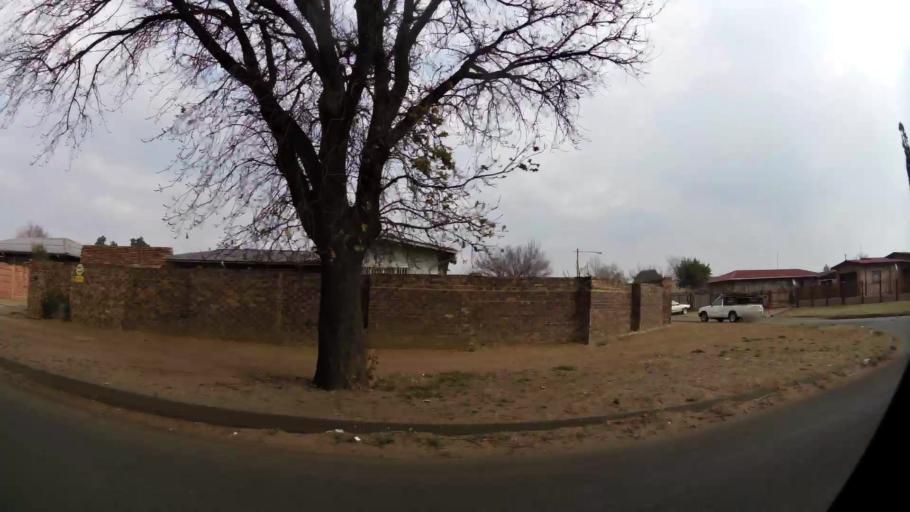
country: ZA
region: Gauteng
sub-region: Sedibeng District Municipality
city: Vanderbijlpark
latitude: -26.6760
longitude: 27.8374
